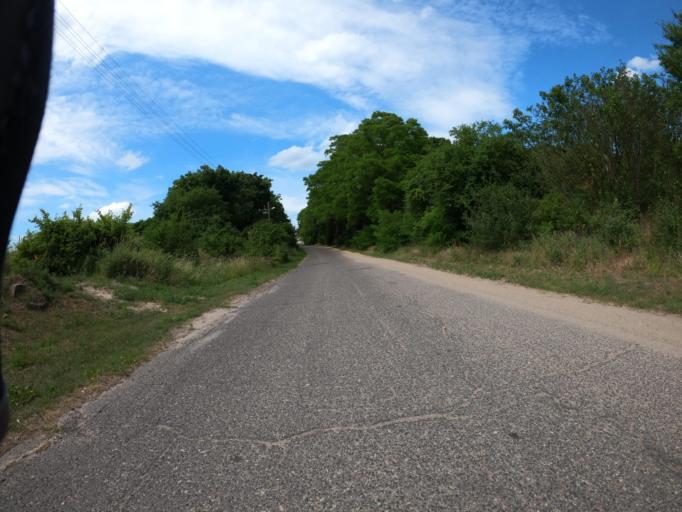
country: DE
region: Brandenburg
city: Letschin
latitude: 52.7342
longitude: 14.3849
